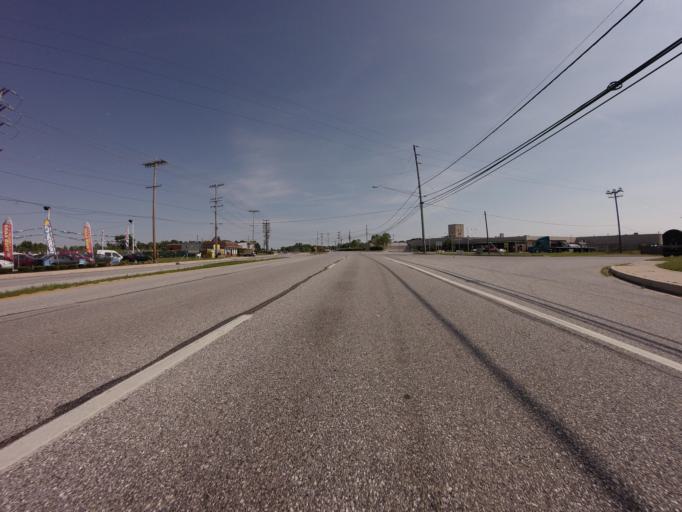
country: US
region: Maryland
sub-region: Baltimore County
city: Edgemere
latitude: 39.2543
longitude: -76.4616
